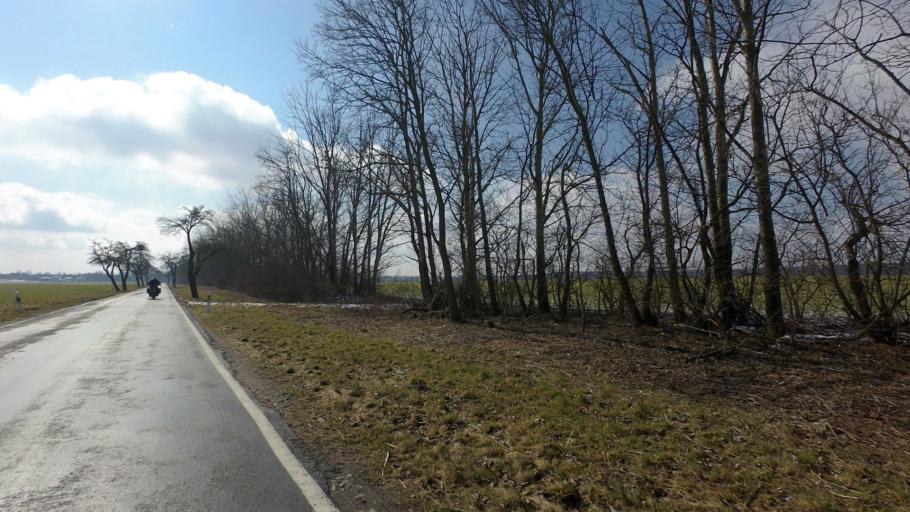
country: DE
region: Brandenburg
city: Werneuchen
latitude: 52.6924
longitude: 13.7252
